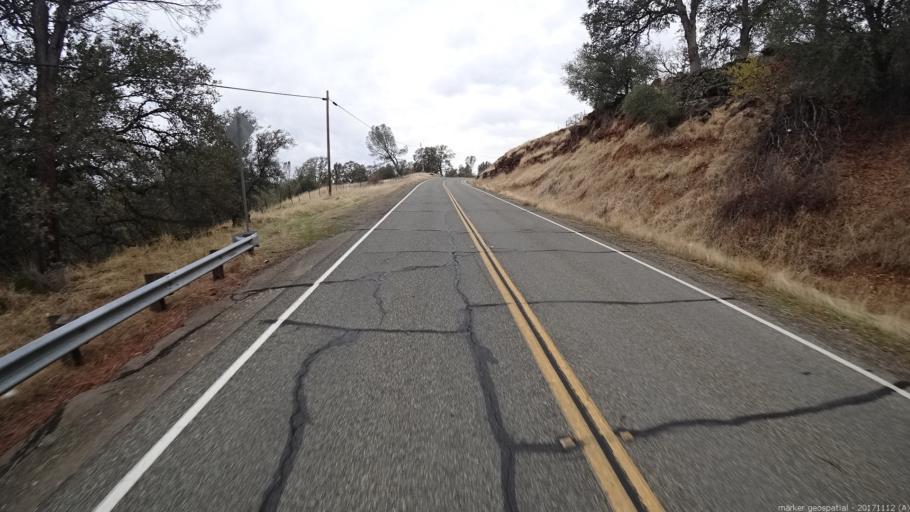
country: US
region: California
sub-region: Shasta County
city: Palo Cedro
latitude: 40.4852
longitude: -122.1542
